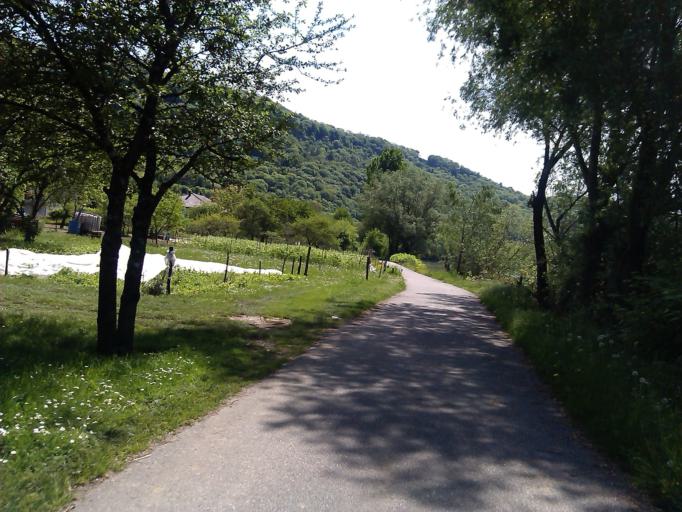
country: FR
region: Franche-Comte
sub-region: Departement du Doubs
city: Beure
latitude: 47.2078
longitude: 5.9954
